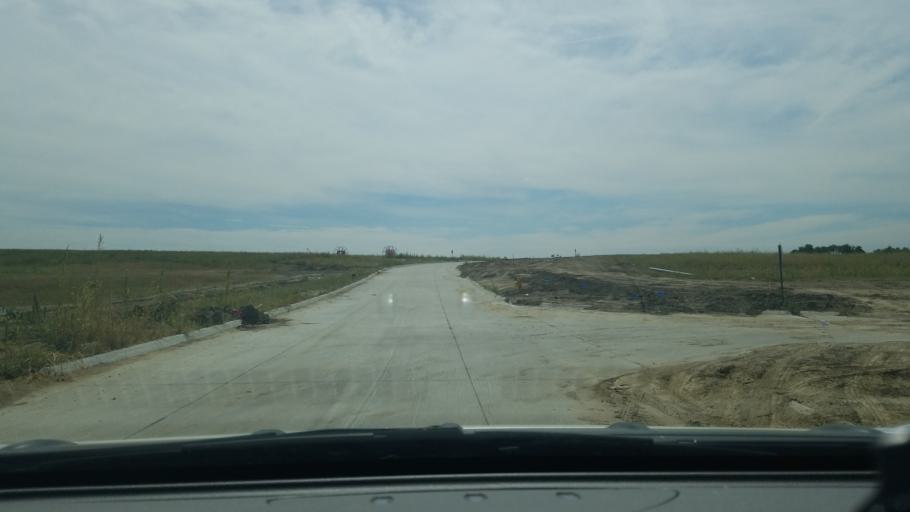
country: US
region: Nebraska
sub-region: Sarpy County
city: Chalco
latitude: 41.1443
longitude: -96.1093
